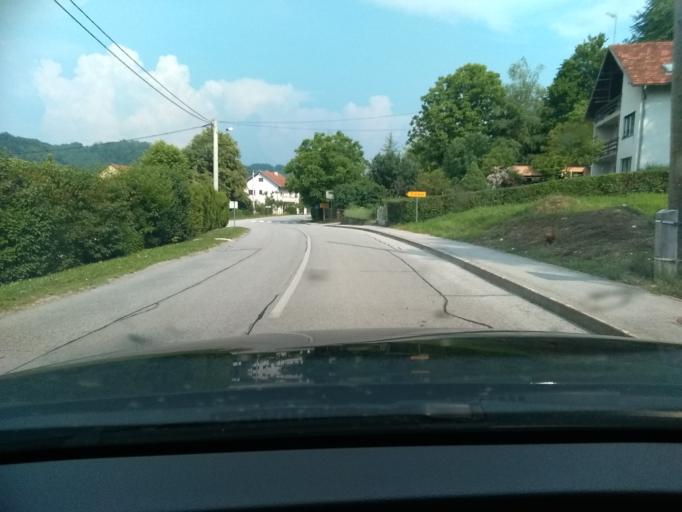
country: HR
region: Krapinsko-Zagorska
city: Pregrada
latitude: 46.0748
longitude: 15.7537
